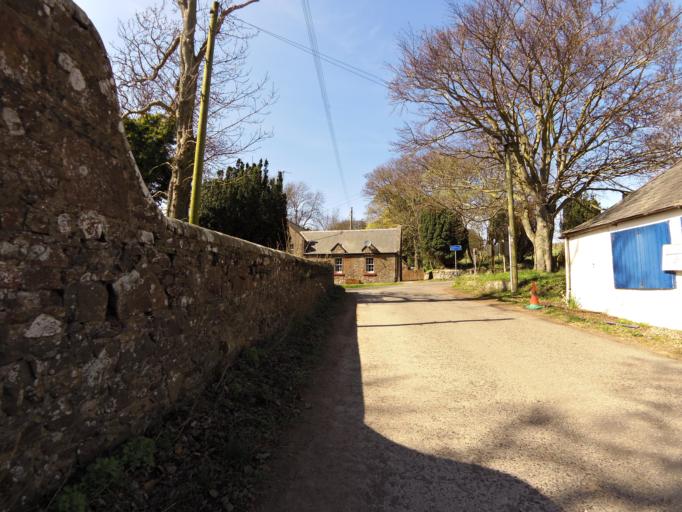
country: GB
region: Scotland
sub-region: Angus
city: Montrose
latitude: 56.6560
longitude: -2.5122
